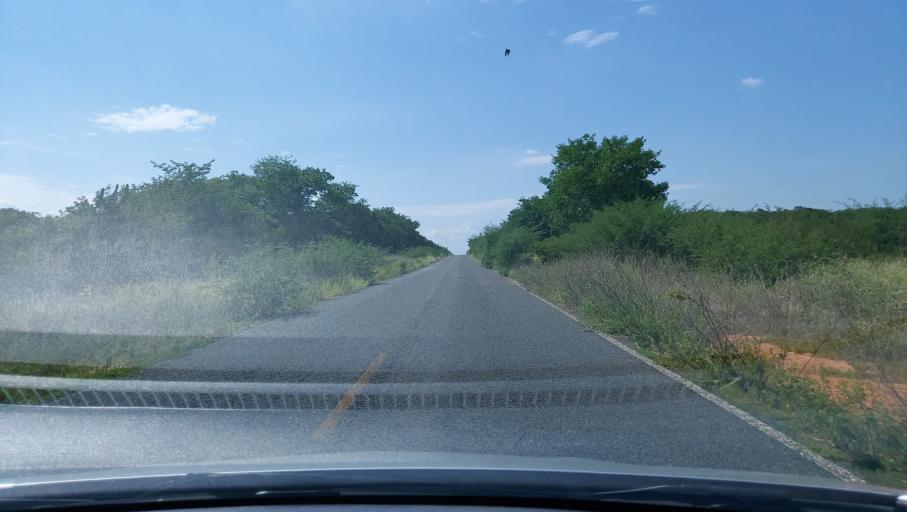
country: BR
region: Bahia
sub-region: Oliveira Dos Brejinhos
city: Beira Rio
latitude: -12.1741
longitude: -42.5445
